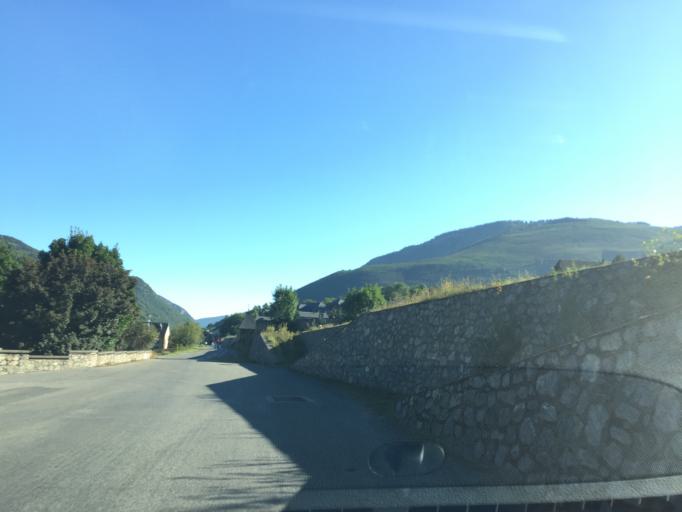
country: FR
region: Midi-Pyrenees
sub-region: Departement des Hautes-Pyrenees
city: Saint-Lary-Soulan
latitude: 42.8989
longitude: 0.3569
